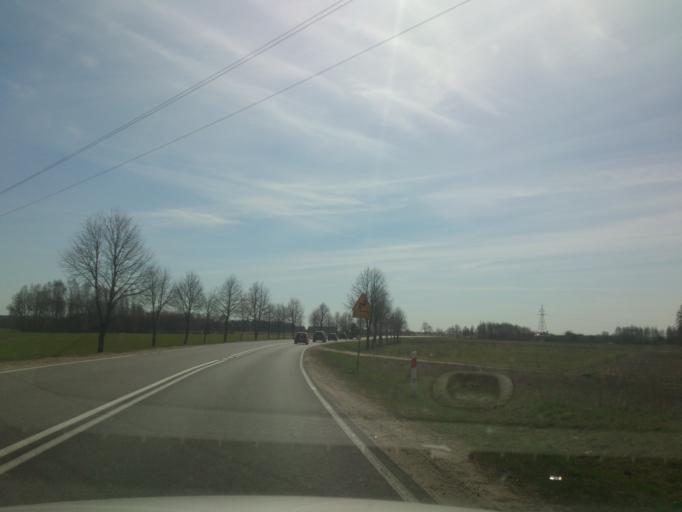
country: PL
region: Masovian Voivodeship
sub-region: Powiat mlawski
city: Szydlowo
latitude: 53.0943
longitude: 20.4184
